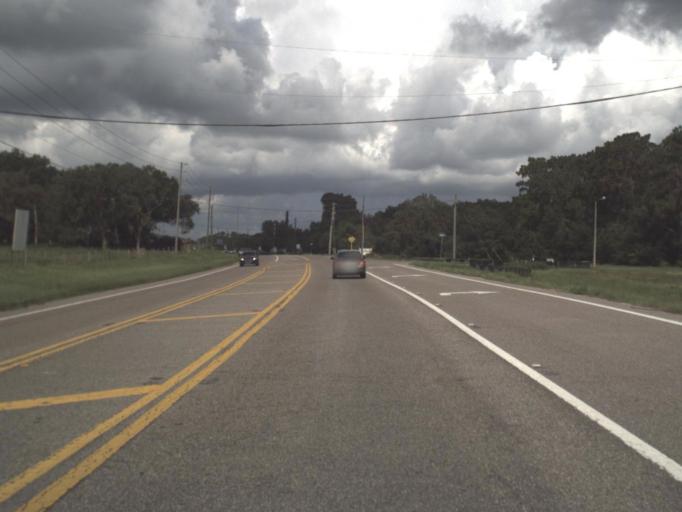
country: US
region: Florida
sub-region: Pasco County
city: San Antonio
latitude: 28.3257
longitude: -82.3164
